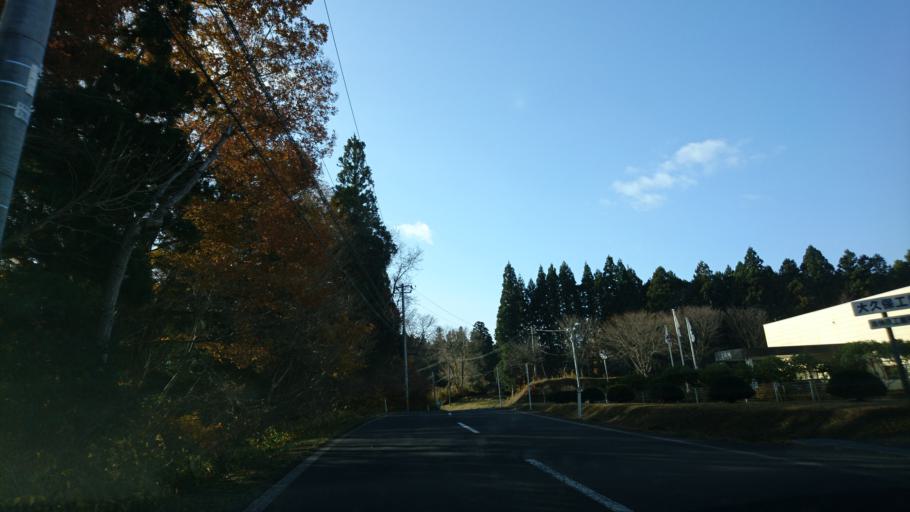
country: JP
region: Iwate
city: Ichinoseki
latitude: 38.8848
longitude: 141.2916
